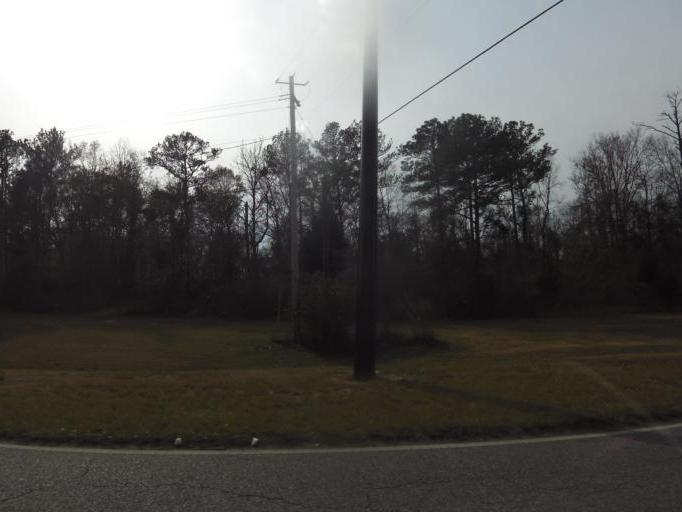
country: US
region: Alabama
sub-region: Houston County
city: Dothan
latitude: 31.2080
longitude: -85.3532
